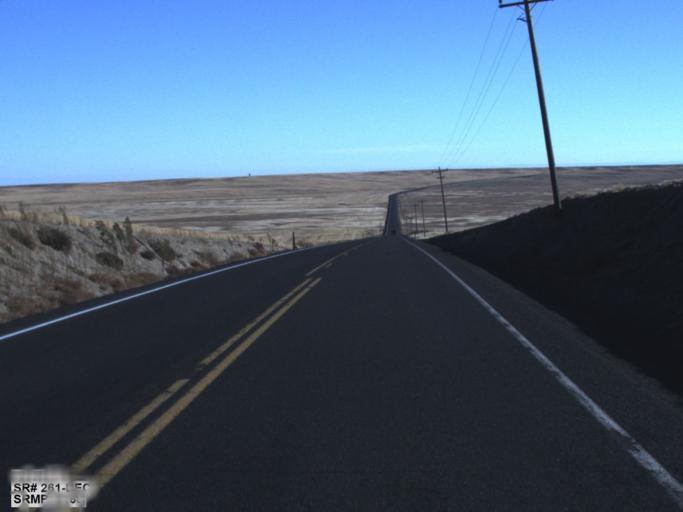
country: US
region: Washington
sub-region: Adams County
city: Ritzville
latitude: 47.0564
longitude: -118.3621
